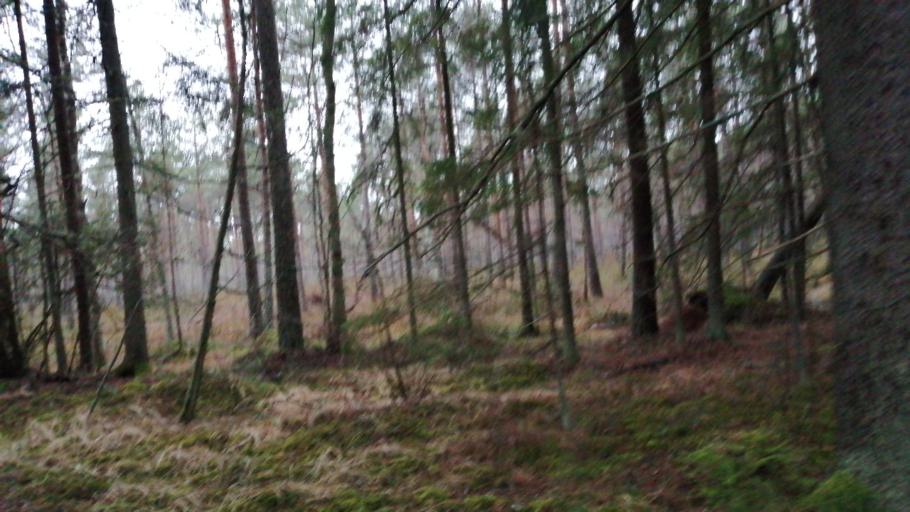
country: EE
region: Polvamaa
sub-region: Polva linn
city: Polva
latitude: 58.1535
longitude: 27.0683
